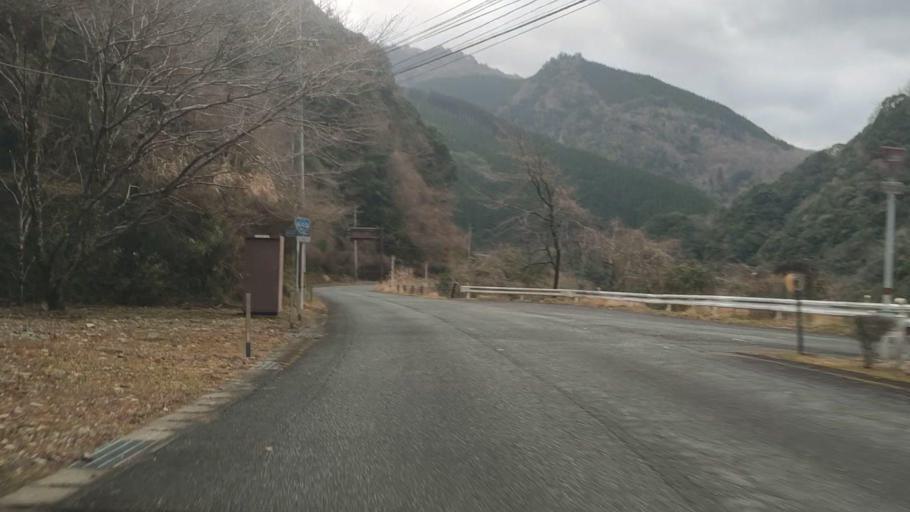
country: JP
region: Kumamoto
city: Matsubase
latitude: 32.5033
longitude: 130.9157
